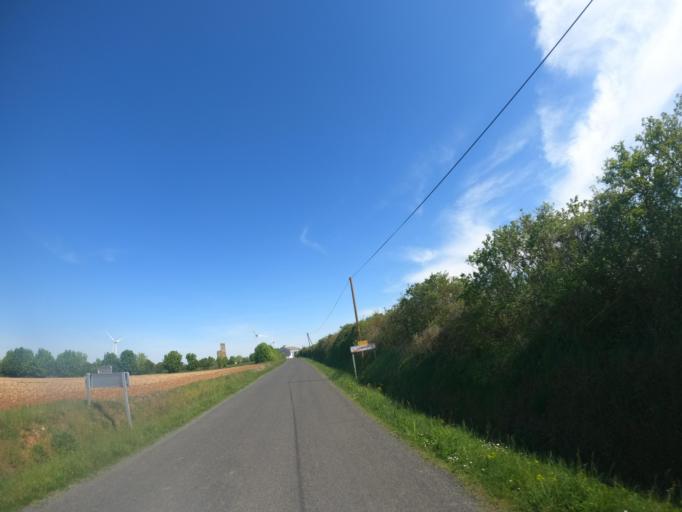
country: FR
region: Poitou-Charentes
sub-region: Departement des Deux-Sevres
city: Airvault
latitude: 46.8840
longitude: -0.1321
